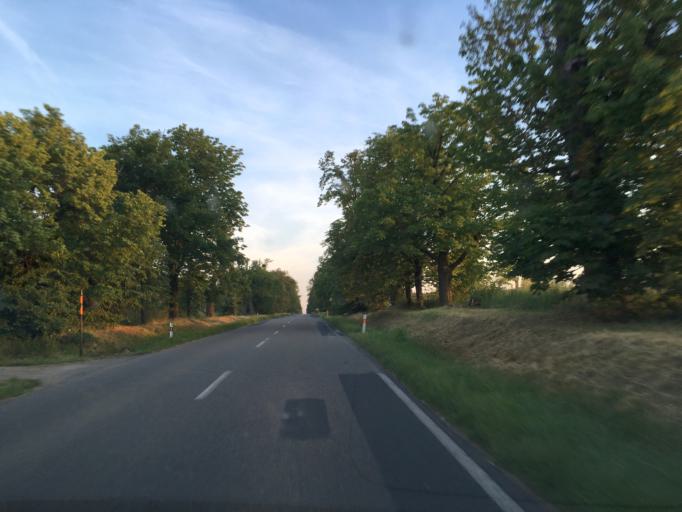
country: CZ
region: South Moravian
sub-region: Okres Breclav
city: Lednice
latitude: 48.7914
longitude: 16.7965
